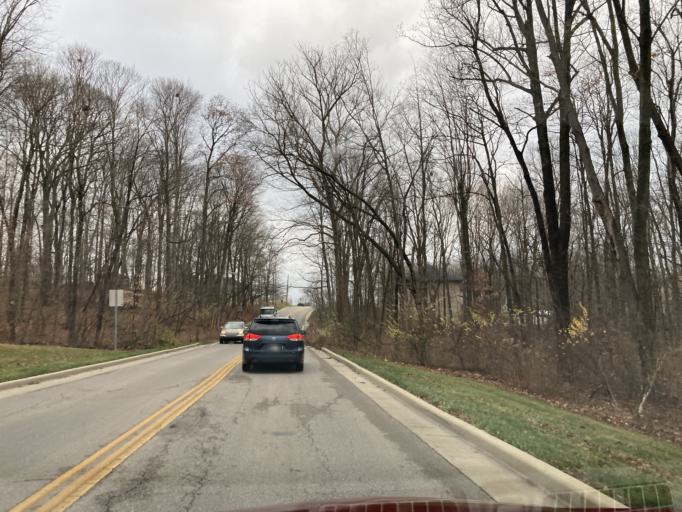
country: US
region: Indiana
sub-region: Monroe County
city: Bloomington
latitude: 39.1793
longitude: -86.5086
